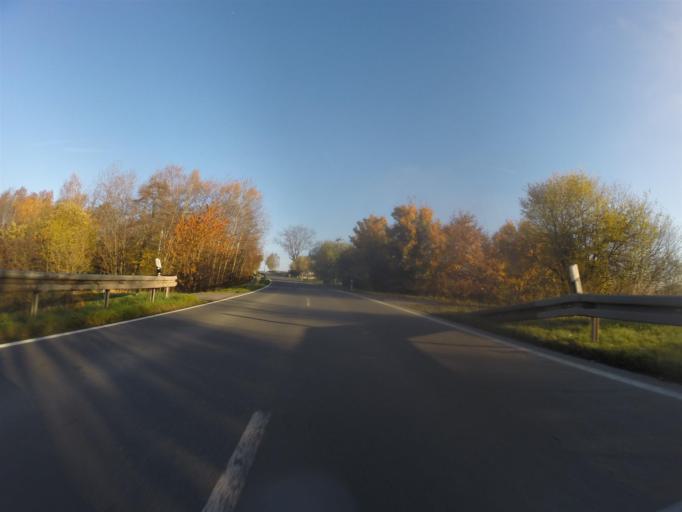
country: DE
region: Thuringia
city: Walpernhain
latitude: 51.0063
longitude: 11.9187
